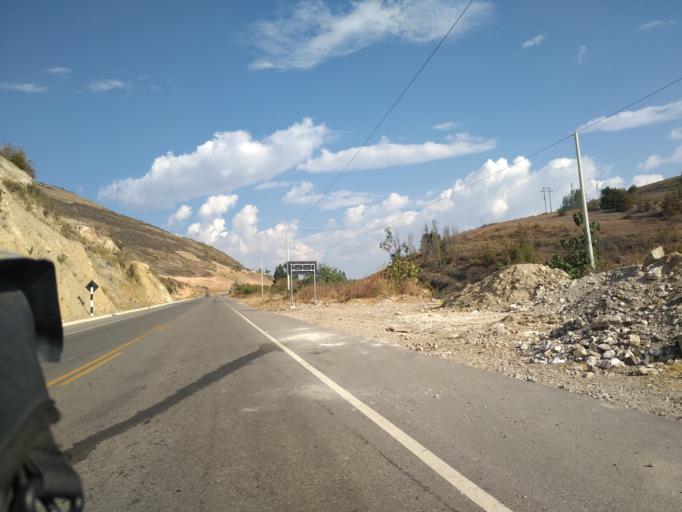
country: PE
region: Cajamarca
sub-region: San Marcos
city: San Marcos
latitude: -7.3770
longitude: -78.1278
